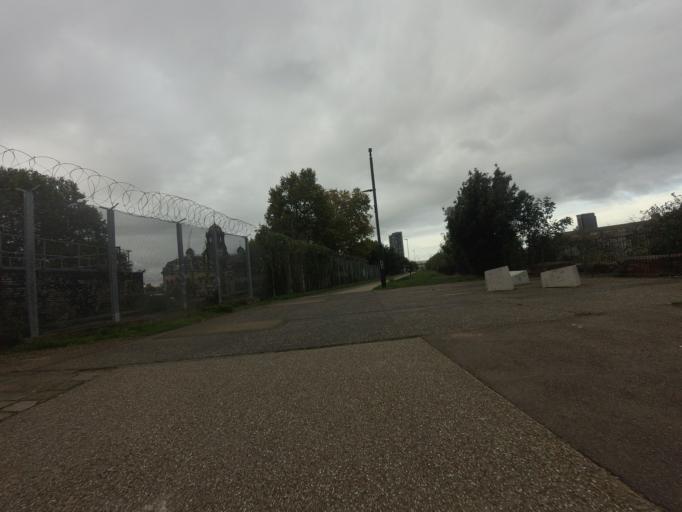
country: GB
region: England
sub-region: Greater London
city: Poplar
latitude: 51.5308
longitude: 0.0003
